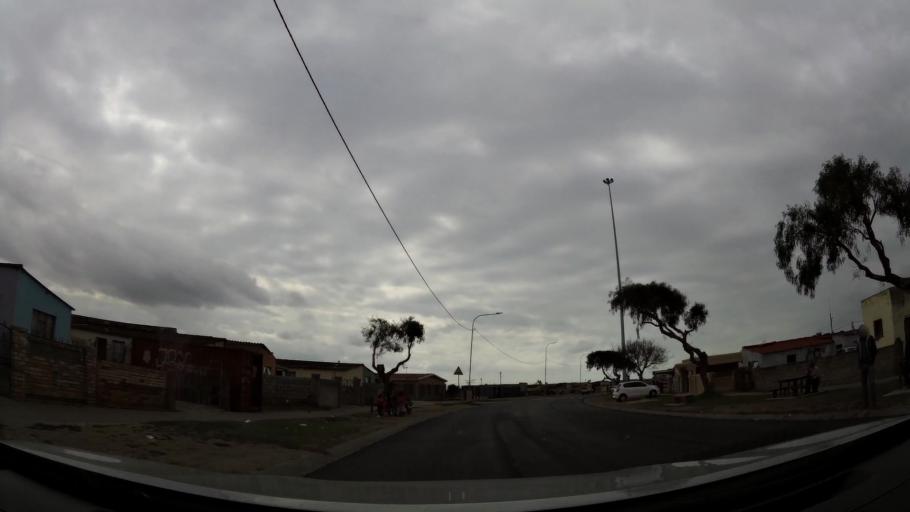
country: ZA
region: Eastern Cape
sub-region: Nelson Mandela Bay Metropolitan Municipality
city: Port Elizabeth
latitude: -33.8923
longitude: 25.5929
